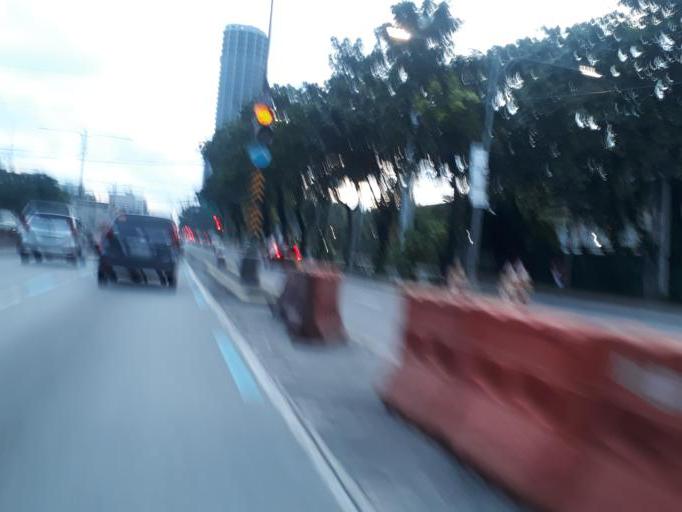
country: PH
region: Metro Manila
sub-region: Quezon City
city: Quezon City
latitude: 14.6475
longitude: 121.0427
